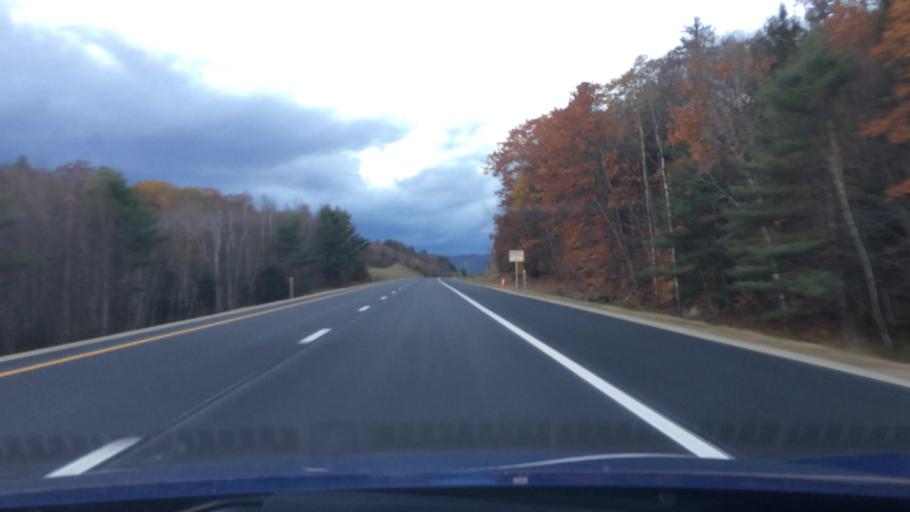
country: US
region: New Hampshire
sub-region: Grafton County
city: Thornton
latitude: 43.8843
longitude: -71.6785
